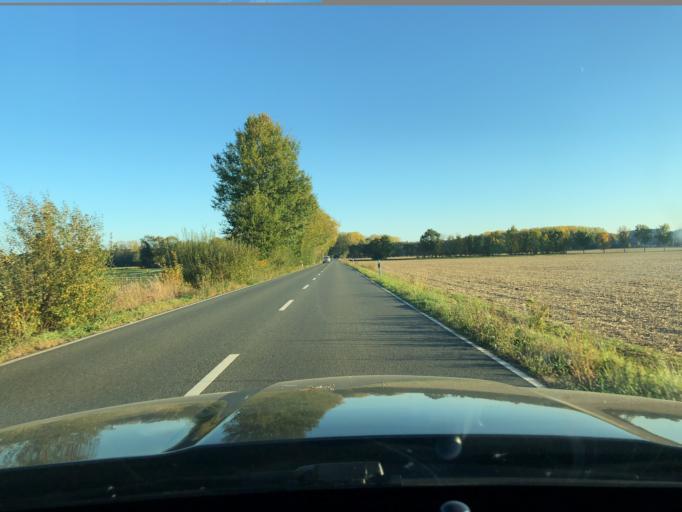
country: DE
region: North Rhine-Westphalia
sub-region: Regierungsbezirk Munster
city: Telgte
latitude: 51.9890
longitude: 7.7140
